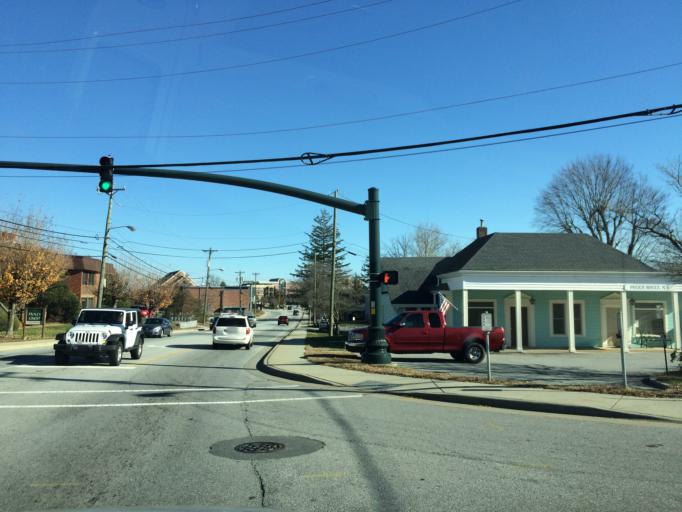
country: US
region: North Carolina
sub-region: Henderson County
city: Hendersonville
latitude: 35.3191
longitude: -82.4665
